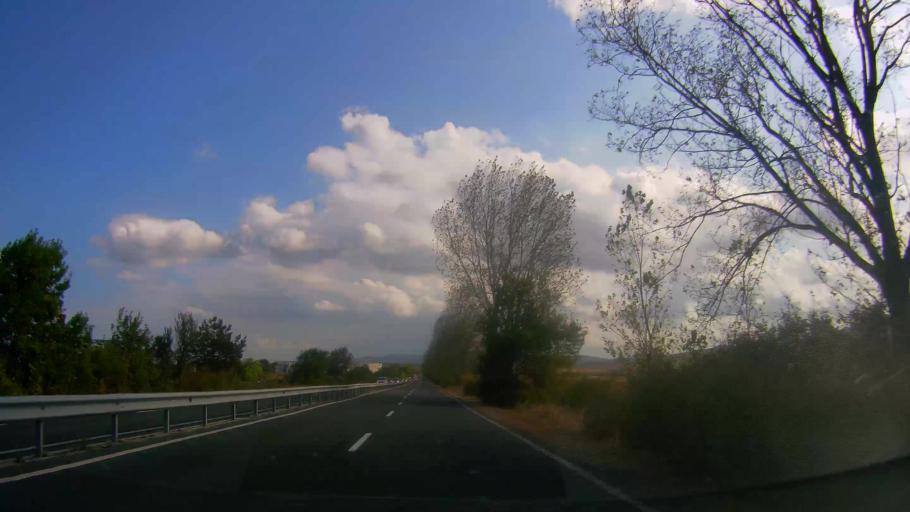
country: BG
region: Burgas
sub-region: Obshtina Sozopol
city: Chernomorets
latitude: 42.4265
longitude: 27.6406
